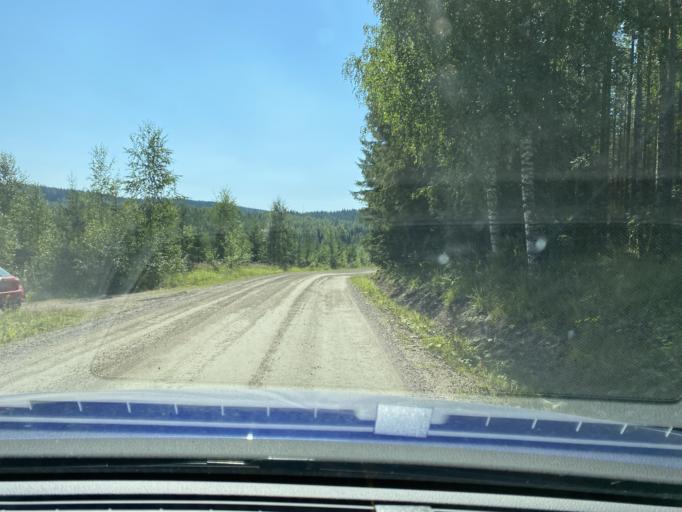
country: FI
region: Central Finland
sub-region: Jyvaeskylae
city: Korpilahti
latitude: 61.8672
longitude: 25.4235
